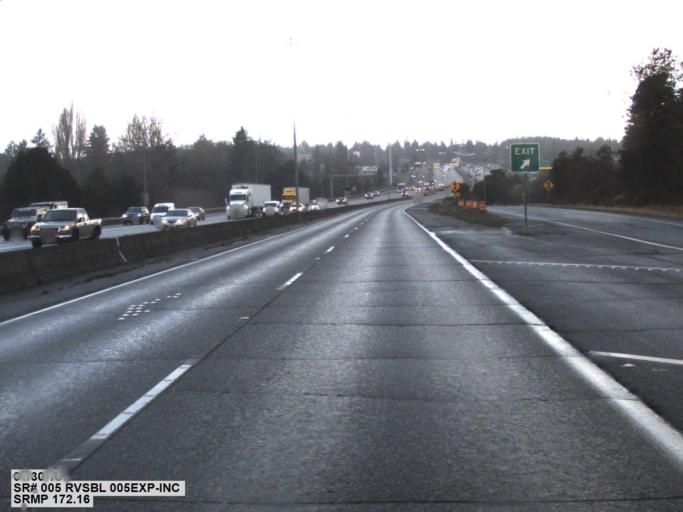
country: US
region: Washington
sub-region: Clark County
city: Salmon Creek
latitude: 45.7129
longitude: -122.6529
